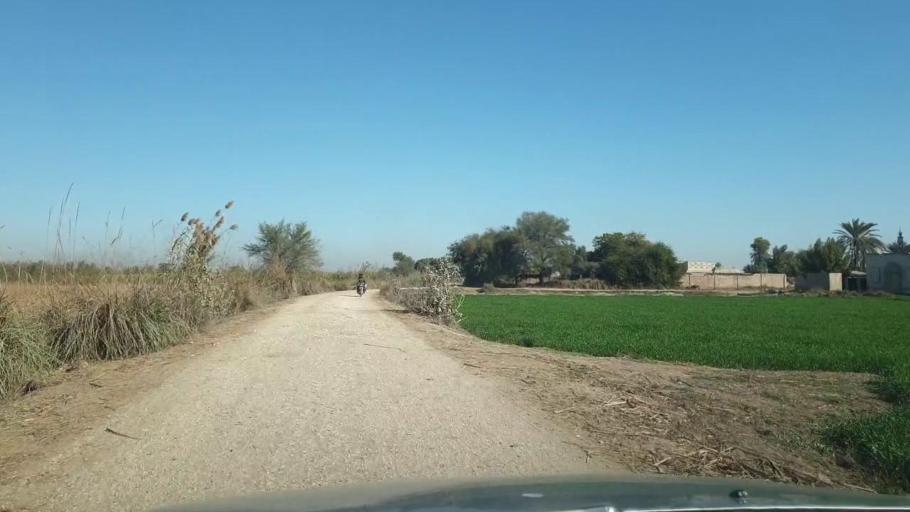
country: PK
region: Sindh
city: Ghotki
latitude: 28.0252
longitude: 69.2858
